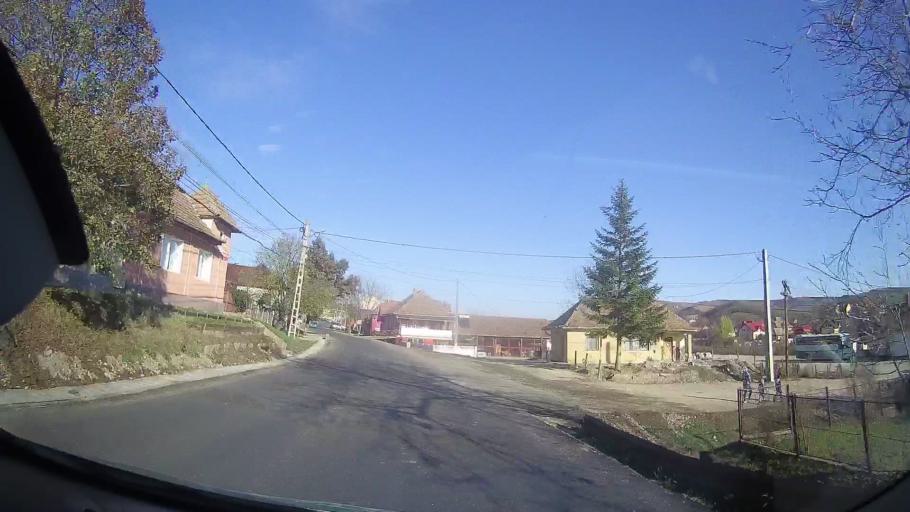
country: RO
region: Mures
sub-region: Comuna Zau De Campie
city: Zau de Campie
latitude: 46.6134
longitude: 24.1241
